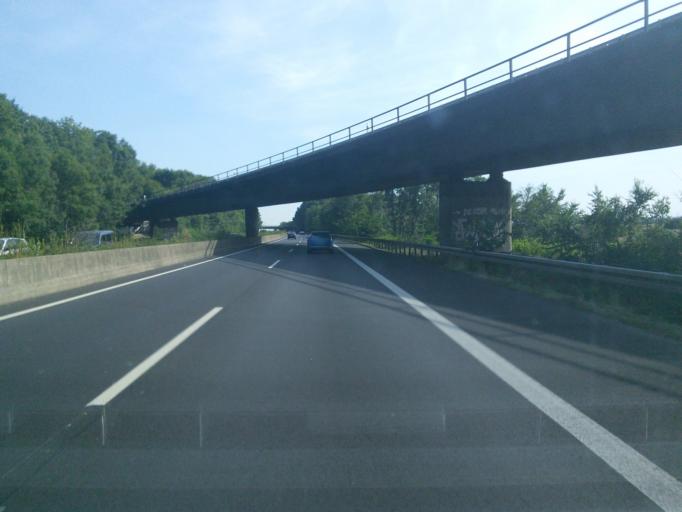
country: DE
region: North Rhine-Westphalia
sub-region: Regierungsbezirk Koln
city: Sinnersdorf
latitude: 51.0438
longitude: 6.8355
